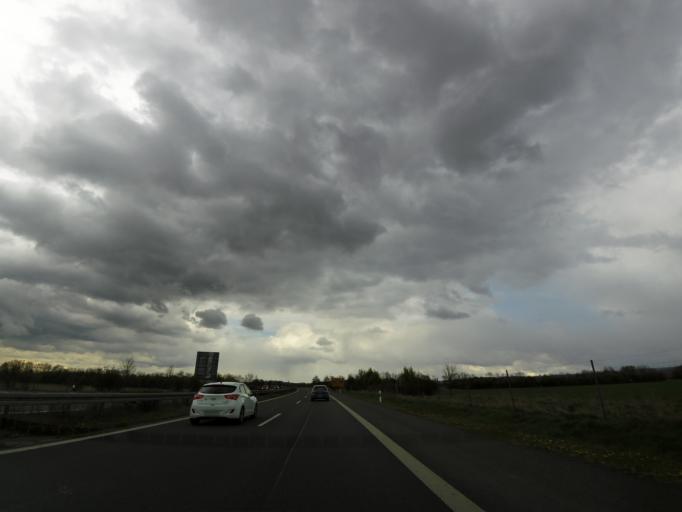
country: DE
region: Saxony-Anhalt
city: Veckenstedt
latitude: 51.8833
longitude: 10.7217
